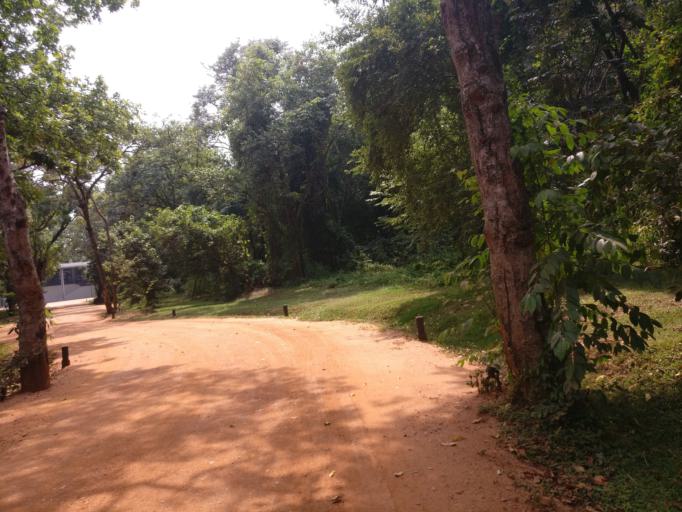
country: LK
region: Central
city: Dambulla
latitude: 7.8403
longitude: 80.6476
